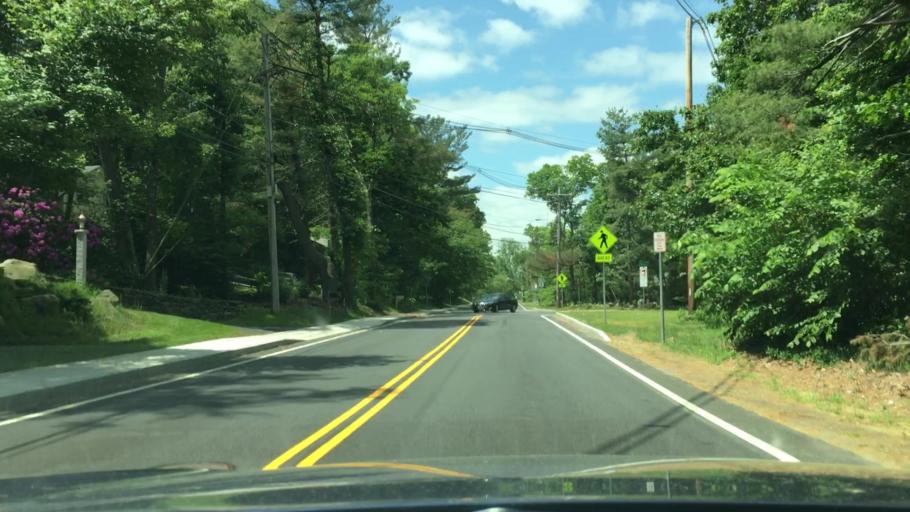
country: US
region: Massachusetts
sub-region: Middlesex County
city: Billerica
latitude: 42.5728
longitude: -71.2695
